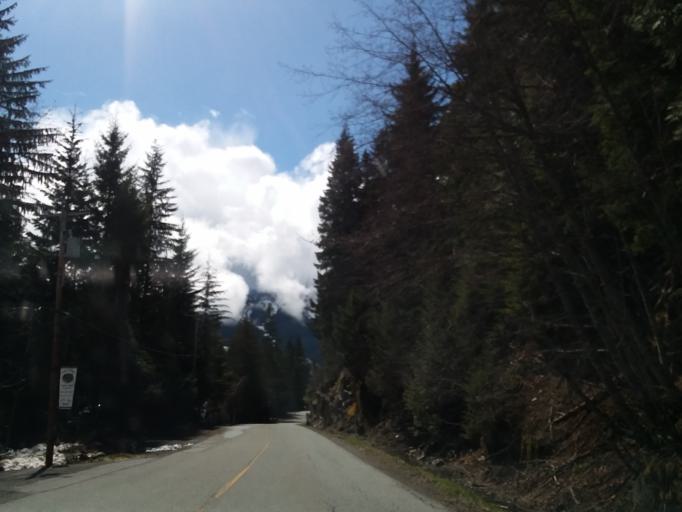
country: CA
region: British Columbia
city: Whistler
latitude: 50.1152
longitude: -122.9863
